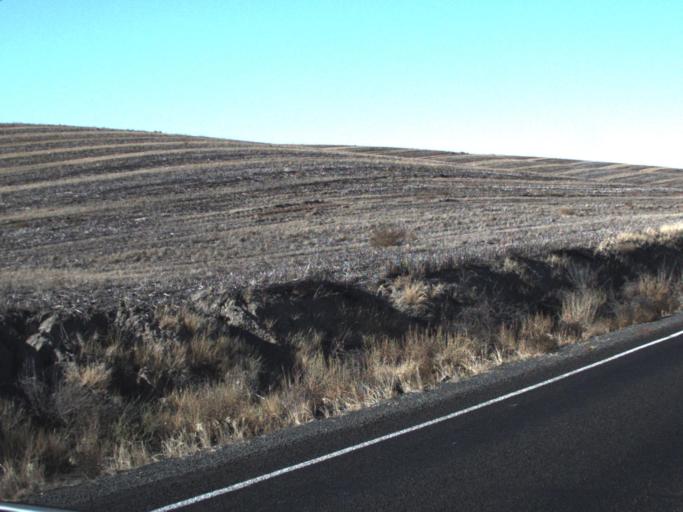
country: US
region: Washington
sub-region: Walla Walla County
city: Walla Walla
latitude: 46.1222
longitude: -118.3722
